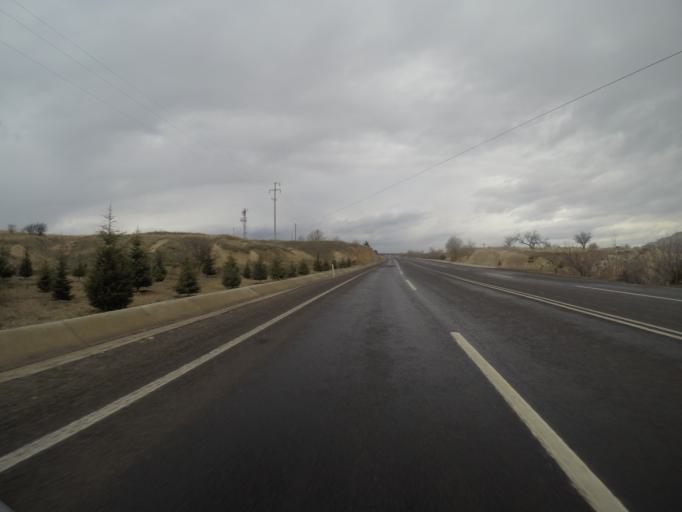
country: TR
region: Nevsehir
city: Urgub
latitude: 38.6346
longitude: 34.8815
